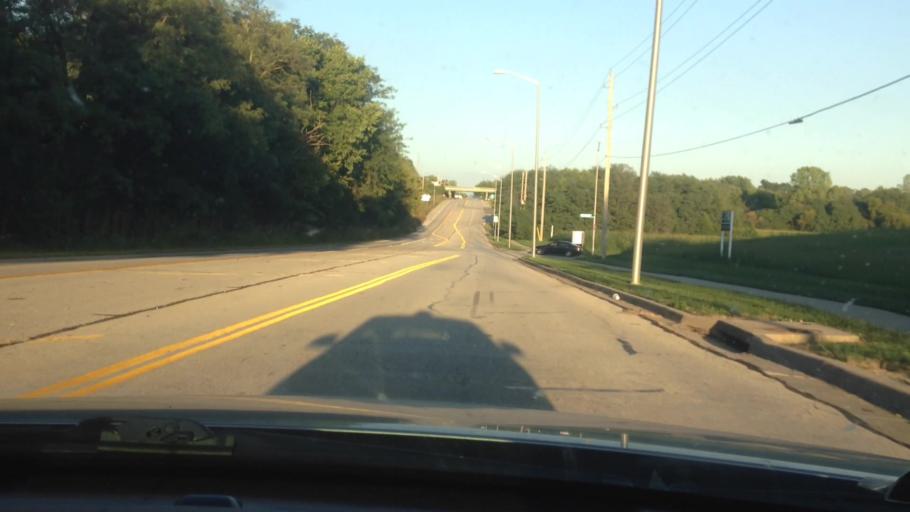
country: US
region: Missouri
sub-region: Clay County
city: Smithville
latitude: 39.3038
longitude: -94.5911
